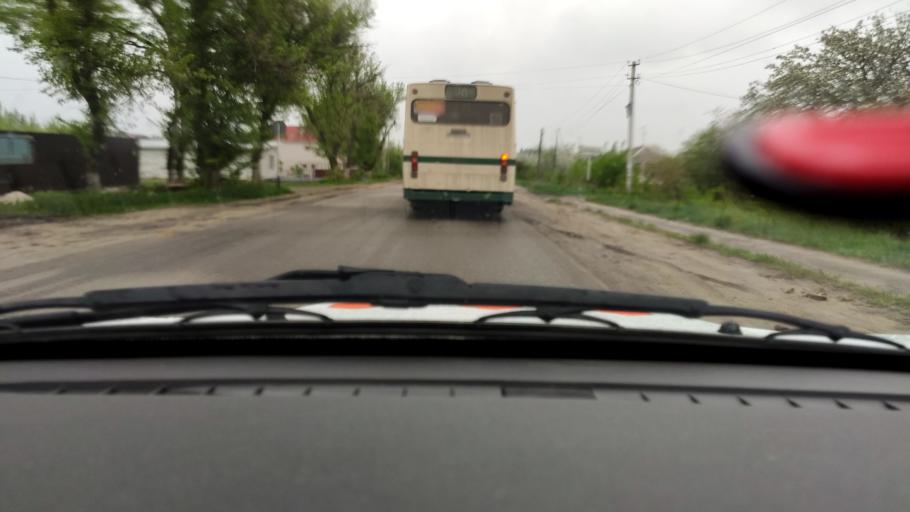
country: RU
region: Voronezj
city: Strelitsa
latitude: 51.6258
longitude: 38.9186
